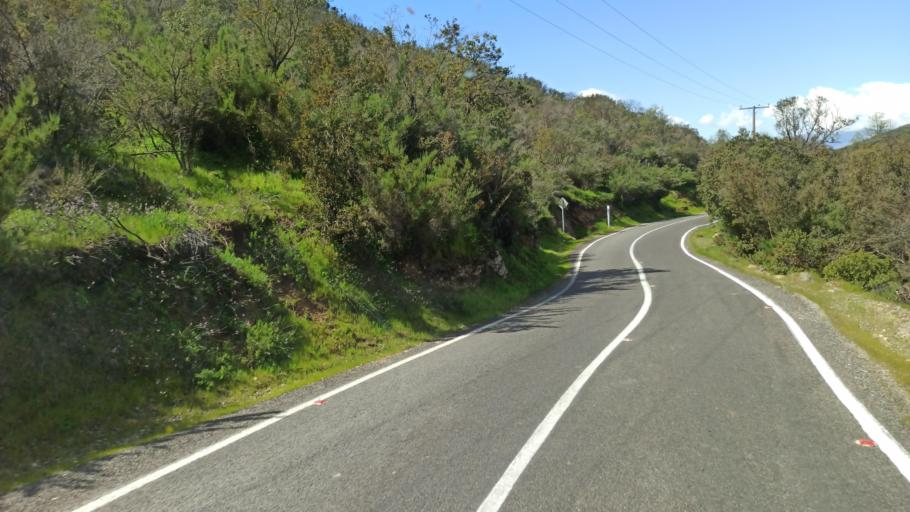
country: CL
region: Valparaiso
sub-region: Provincia de Marga Marga
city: Limache
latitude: -33.1982
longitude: -71.2244
